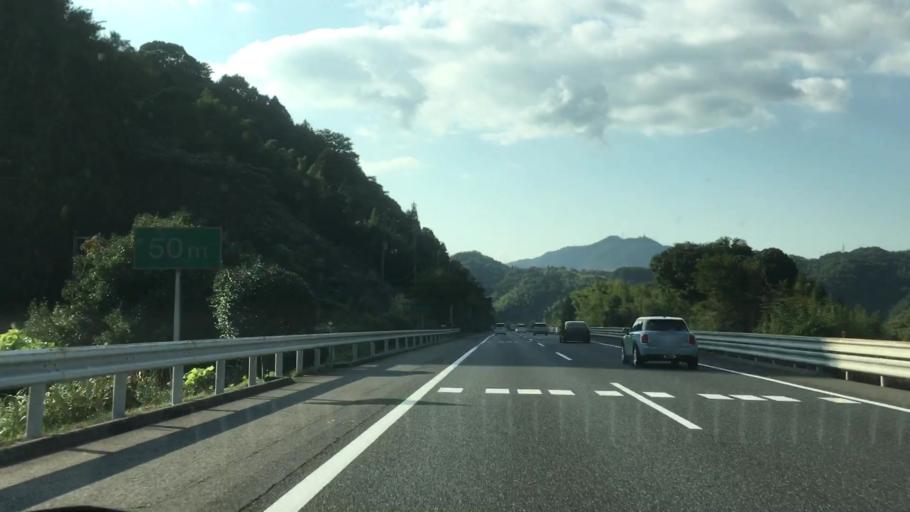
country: JP
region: Yamaguchi
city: Tokuyama
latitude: 34.0748
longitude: 131.8043
